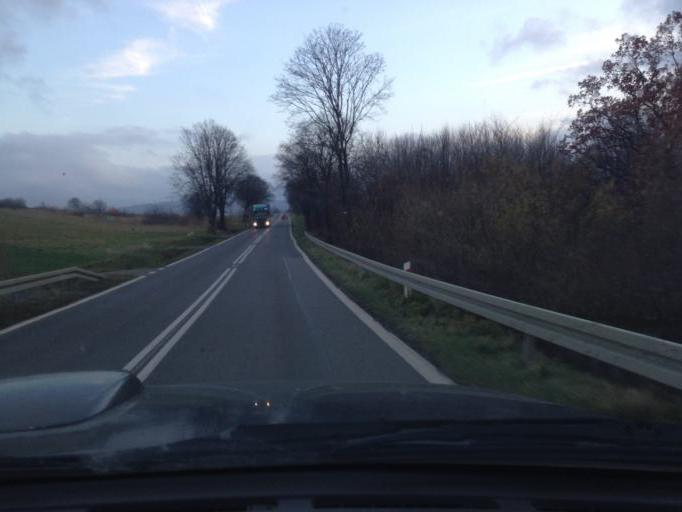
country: PL
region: Subcarpathian Voivodeship
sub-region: Powiat jasielski
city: Nowy Zmigrod
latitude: 49.6290
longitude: 21.5316
